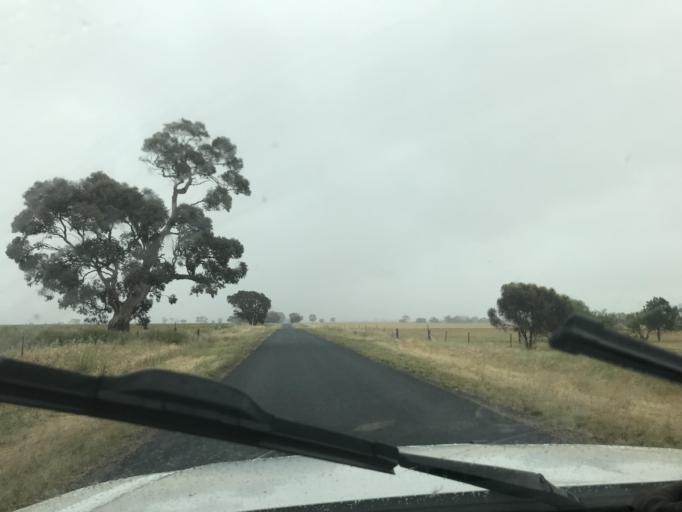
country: AU
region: South Australia
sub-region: Tatiara
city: Bordertown
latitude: -36.3166
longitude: 141.1782
